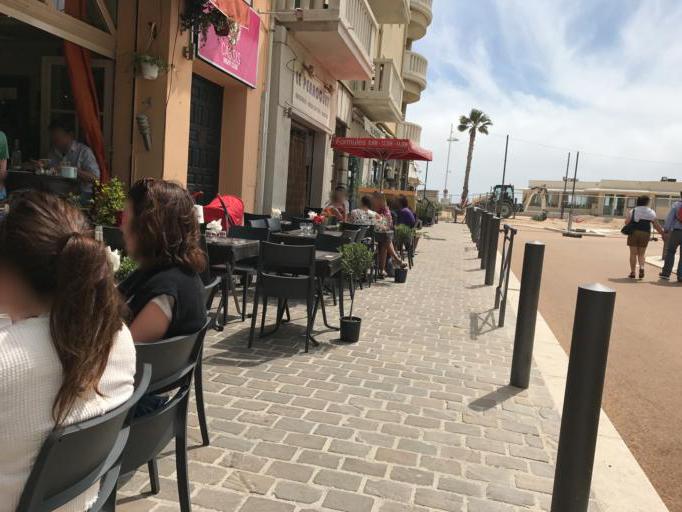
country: FR
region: Provence-Alpes-Cote d'Azur
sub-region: Departement des Bouches-du-Rhone
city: Cassis
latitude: 43.2135
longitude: 5.5387
